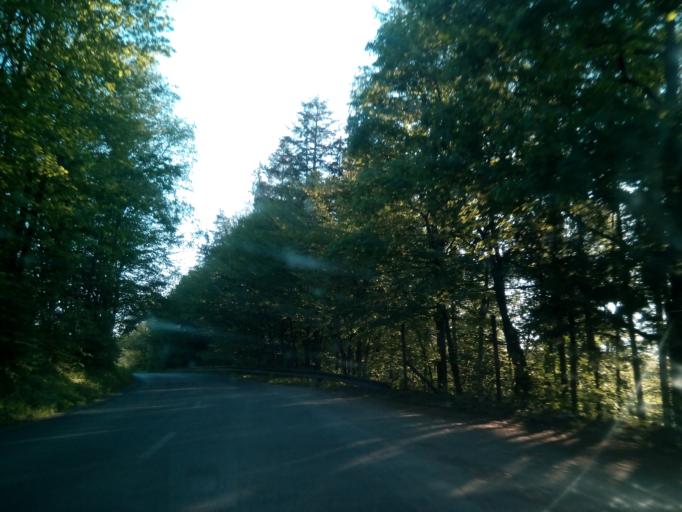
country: CZ
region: South Moravian
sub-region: Okres Blansko
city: Jedovnice
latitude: 49.3336
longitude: 16.7432
